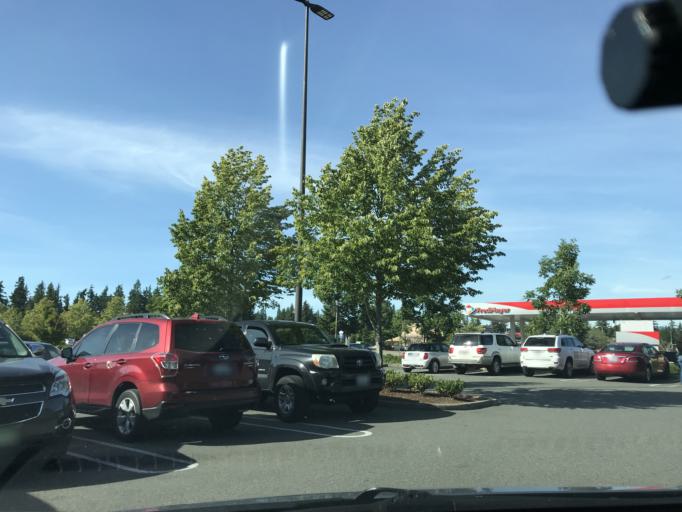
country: US
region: Washington
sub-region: King County
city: Covington
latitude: 47.3558
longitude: -122.1208
